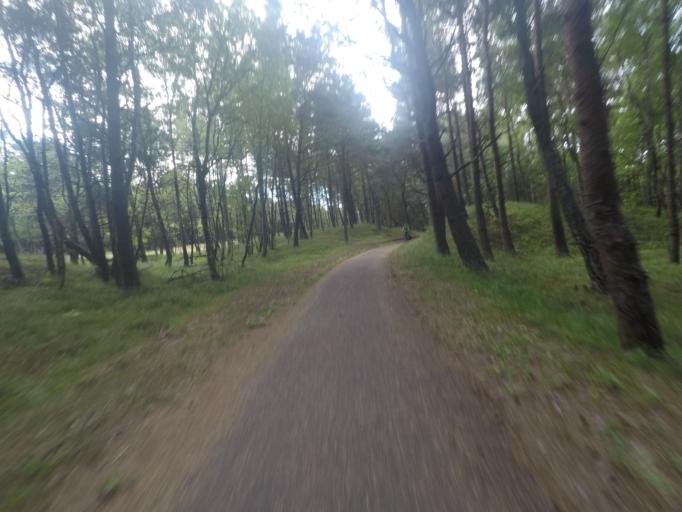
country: LT
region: Klaipedos apskritis
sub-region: Klaipeda
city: Klaipeda
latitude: 55.6525
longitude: 21.1083
